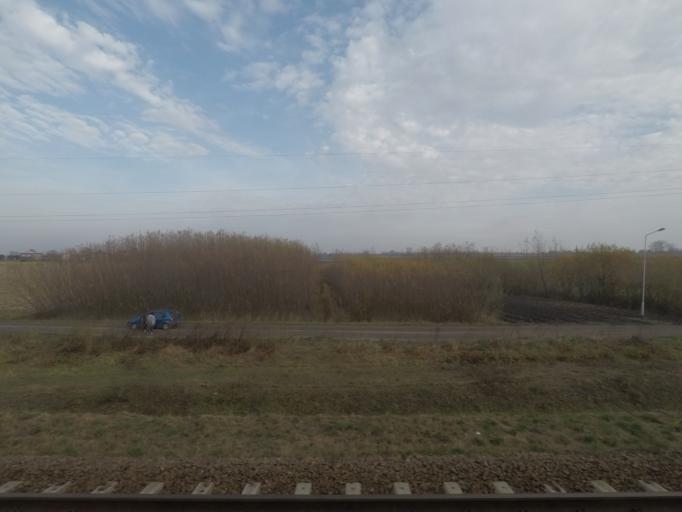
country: PL
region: Subcarpathian Voivodeship
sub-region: Powiat jaroslawski
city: Sosnica
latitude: 49.9046
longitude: 22.8507
